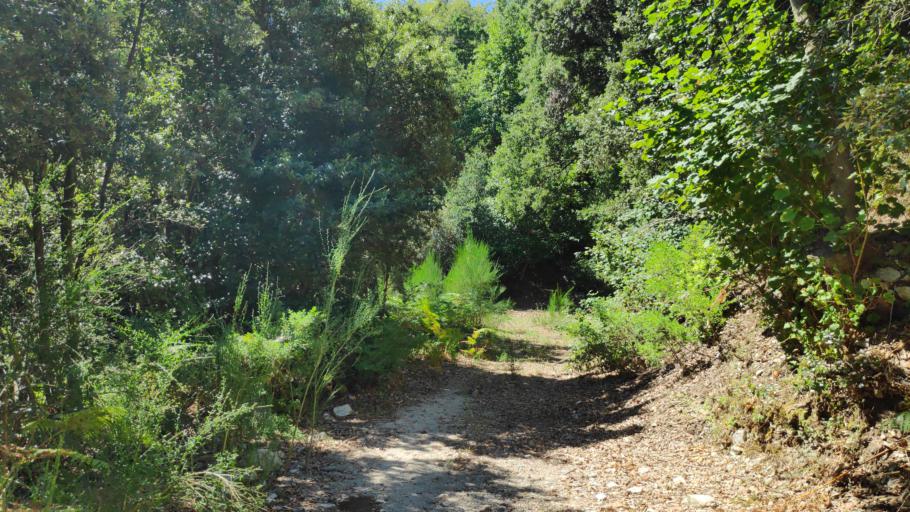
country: IT
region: Calabria
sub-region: Provincia di Vibo-Valentia
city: Nardodipace
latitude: 38.4804
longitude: 16.3830
